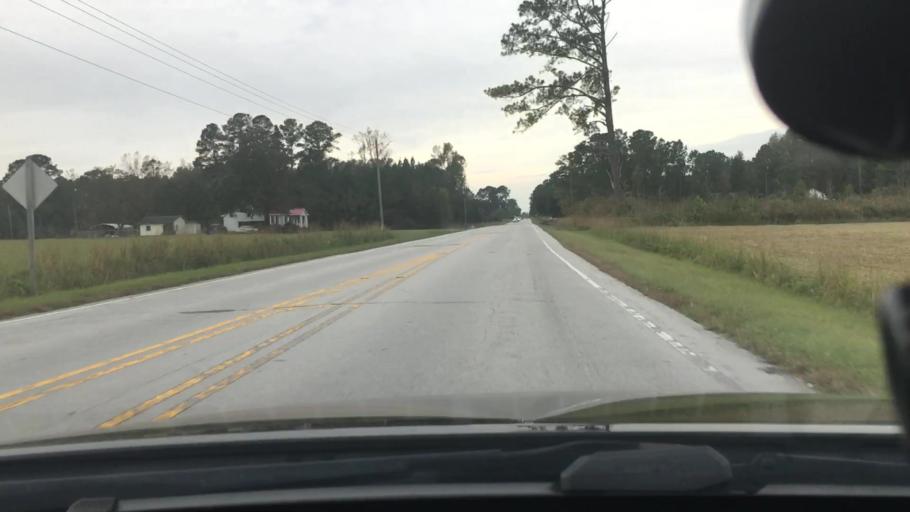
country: US
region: North Carolina
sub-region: Craven County
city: Vanceboro
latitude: 35.3539
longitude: -77.1908
